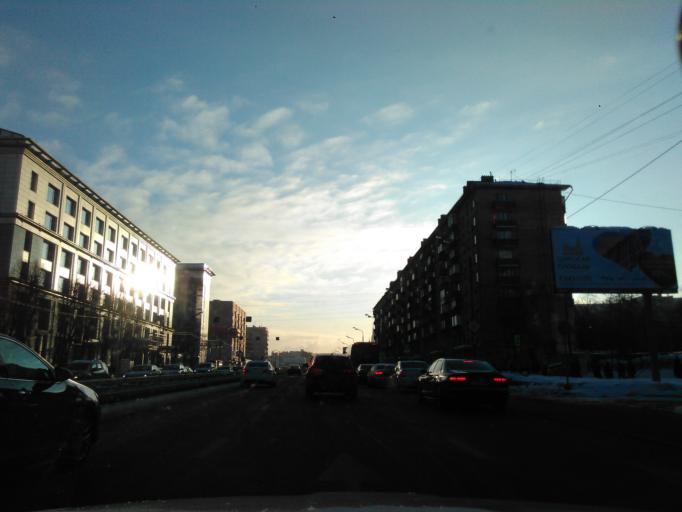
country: RU
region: Moskovskaya
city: Presnenskiy
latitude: 55.7641
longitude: 37.5543
